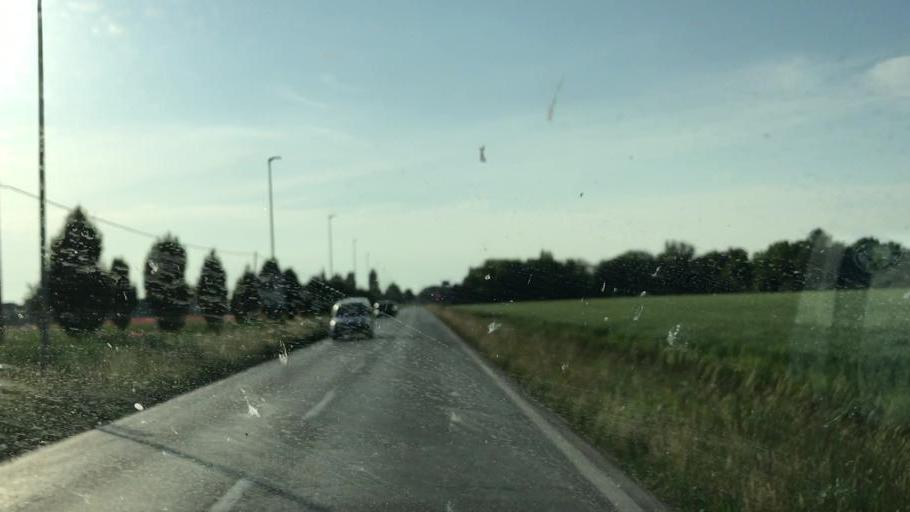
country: IT
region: Lombardy
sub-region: Provincia di Mantova
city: Casaloldo
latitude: 45.2491
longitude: 10.4891
